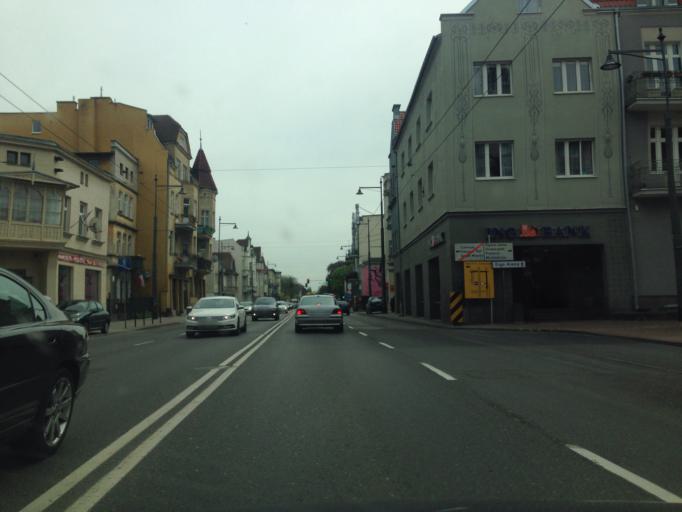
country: PL
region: Pomeranian Voivodeship
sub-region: Sopot
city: Sopot
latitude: 54.4432
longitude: 18.5597
